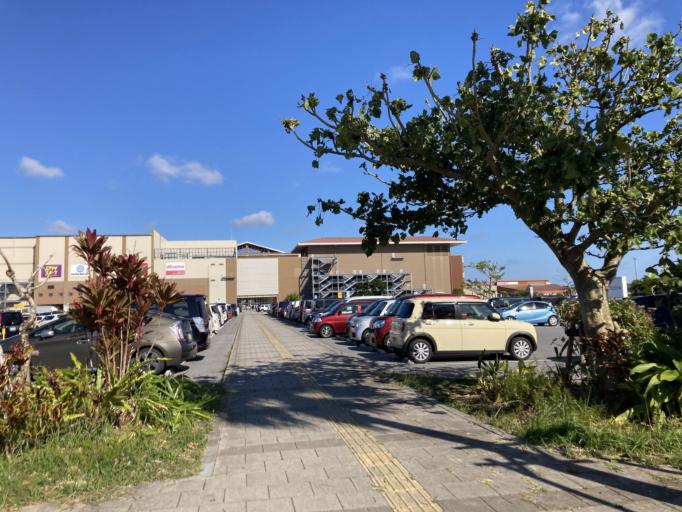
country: JP
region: Okinawa
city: Okinawa
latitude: 26.3120
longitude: 127.7966
